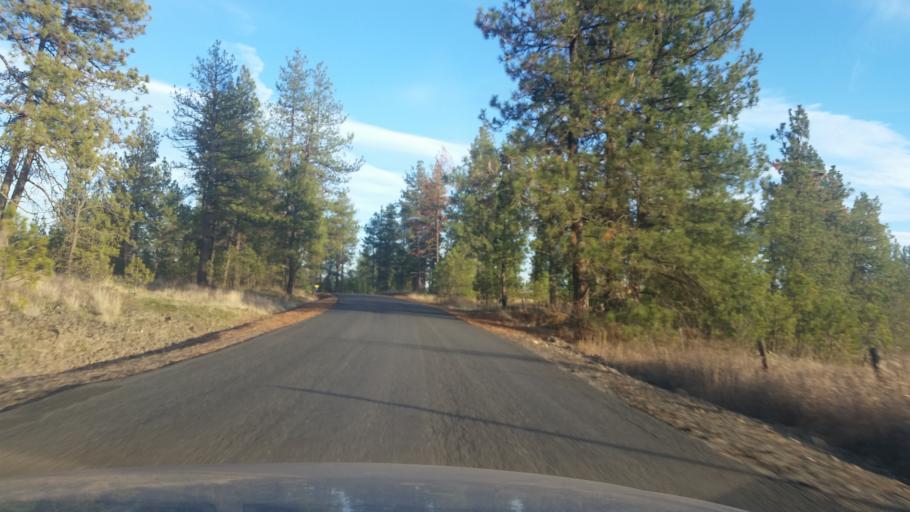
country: US
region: Washington
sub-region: Spokane County
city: Cheney
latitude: 47.5152
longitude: -117.4763
